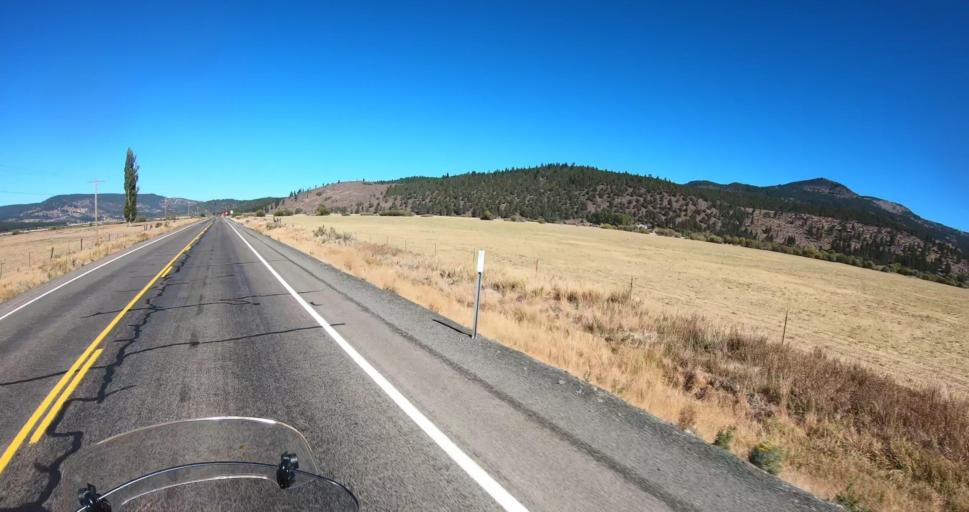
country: US
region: Oregon
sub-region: Lake County
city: Lakeview
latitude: 42.3366
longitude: -120.2975
